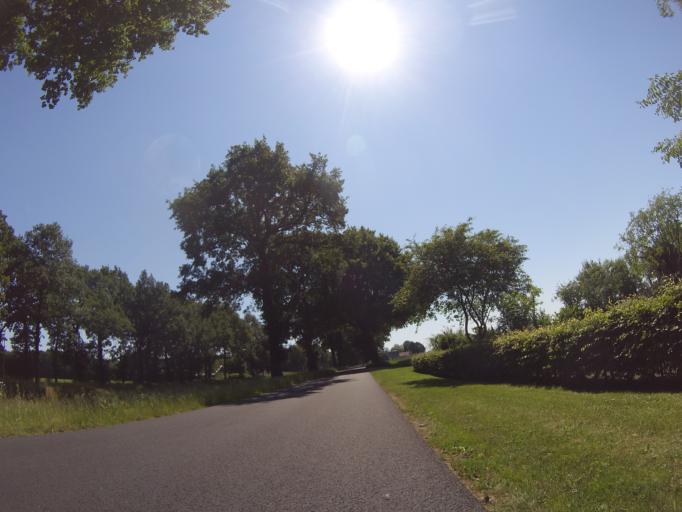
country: NL
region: Drenthe
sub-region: Gemeente Coevorden
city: Sleen
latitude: 52.8381
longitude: 6.7973
